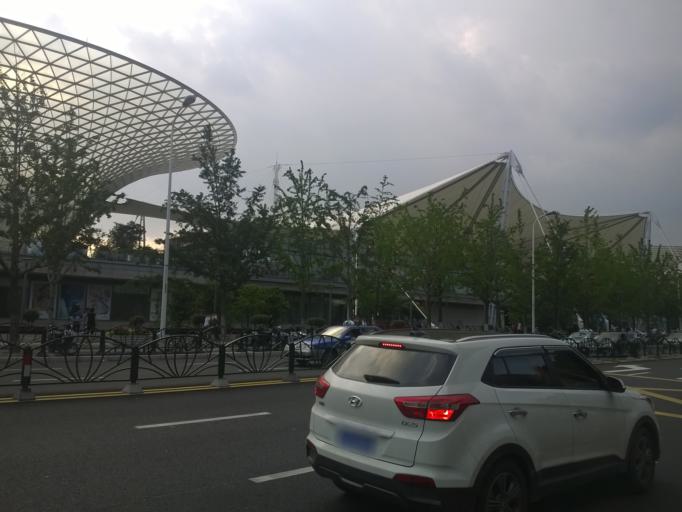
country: CN
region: Shanghai Shi
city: Luwan
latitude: 31.1860
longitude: 121.4890
